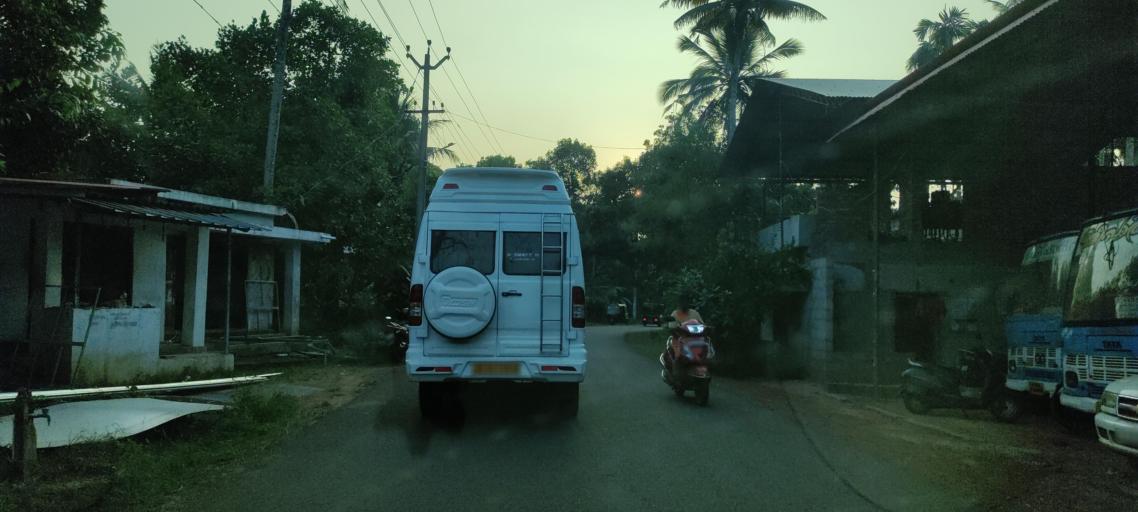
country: IN
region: Kerala
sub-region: Alappuzha
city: Kattanam
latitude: 9.1411
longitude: 76.5627
